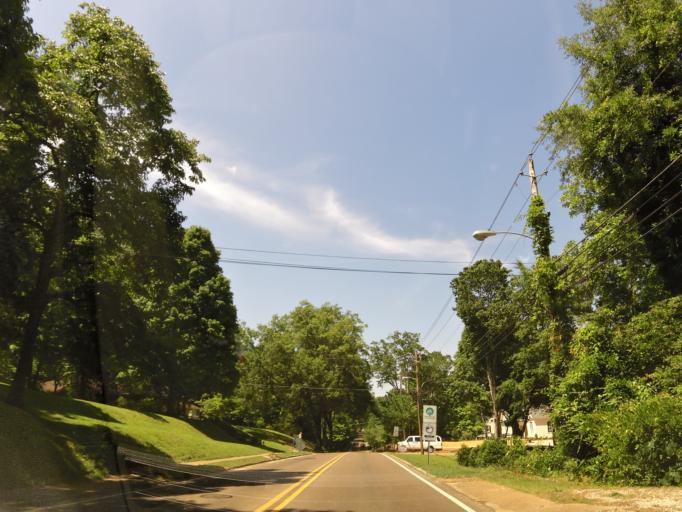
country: US
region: Mississippi
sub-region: Lafayette County
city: Oxford
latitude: 34.3567
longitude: -89.5208
